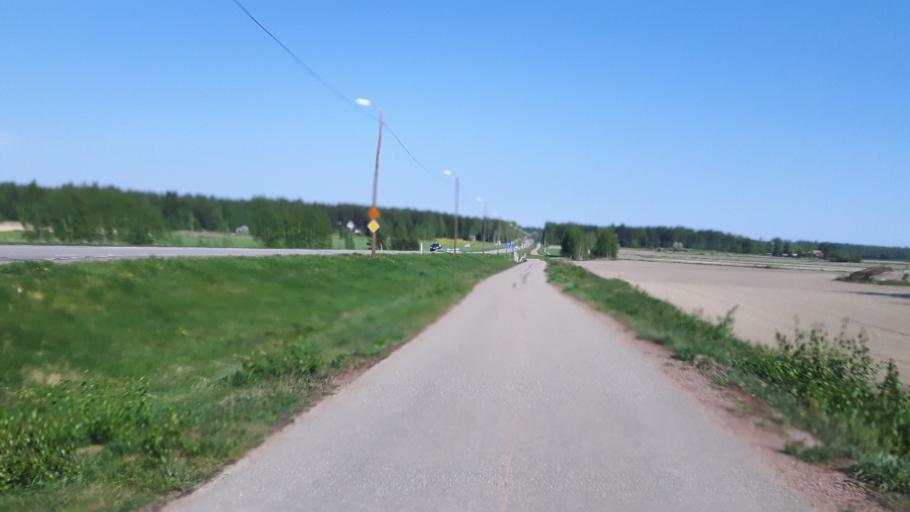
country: FI
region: Kymenlaakso
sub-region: Kotka-Hamina
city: Broby
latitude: 60.4965
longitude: 26.7926
